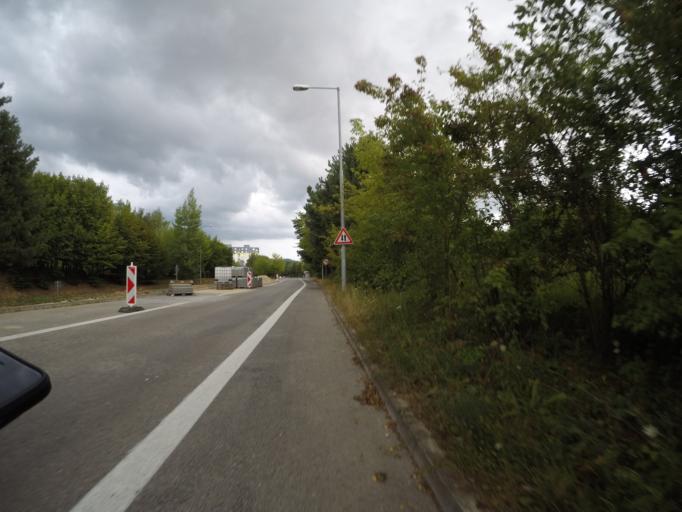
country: SK
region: Trenciansky
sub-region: Okres Trencin
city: Trencin
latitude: 48.8707
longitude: 18.0390
